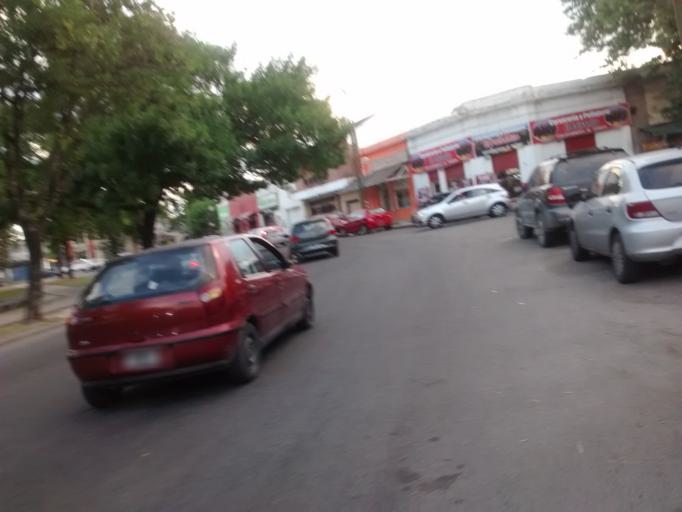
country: AR
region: Buenos Aires
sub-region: Partido de La Plata
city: La Plata
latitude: -34.9319
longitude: -57.9549
